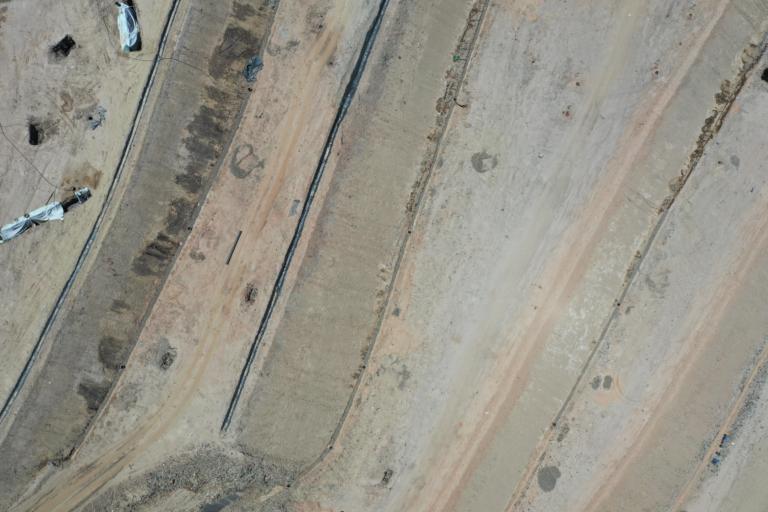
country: BO
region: La Paz
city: La Paz
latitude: -16.5564
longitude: -68.1260
